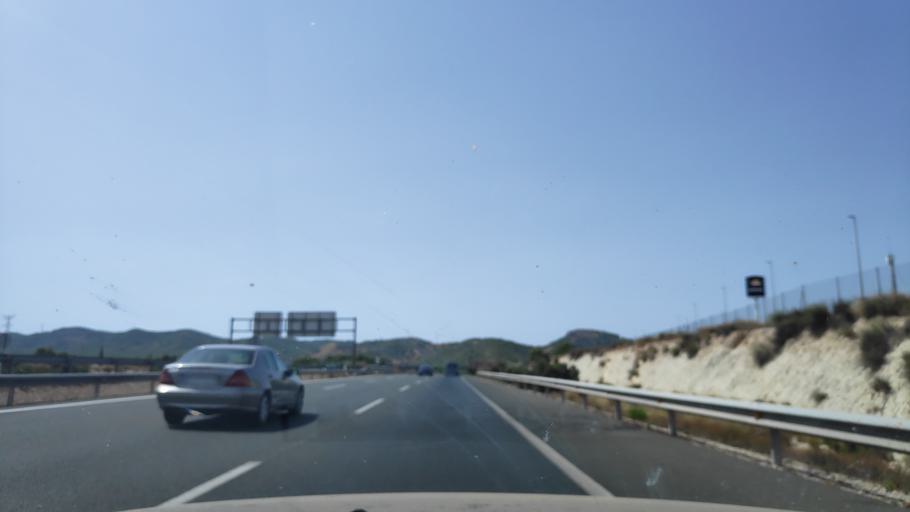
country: ES
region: Murcia
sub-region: Murcia
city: Murcia
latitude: 37.8830
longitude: -1.1352
